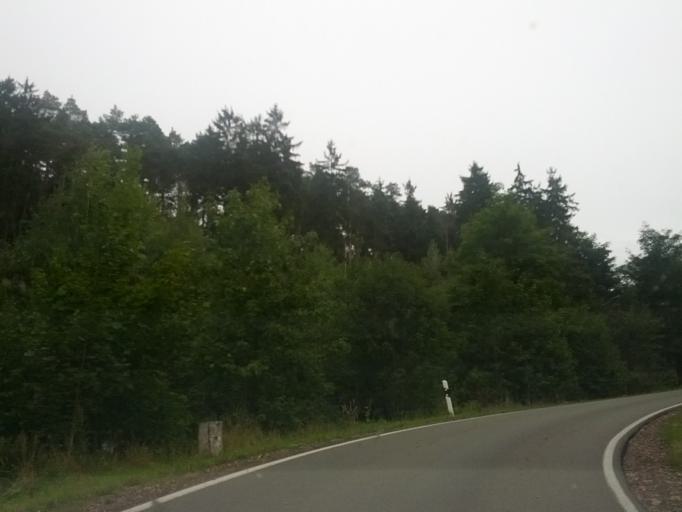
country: DE
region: Thuringia
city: Bad Salzungen
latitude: 50.8351
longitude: 10.2387
